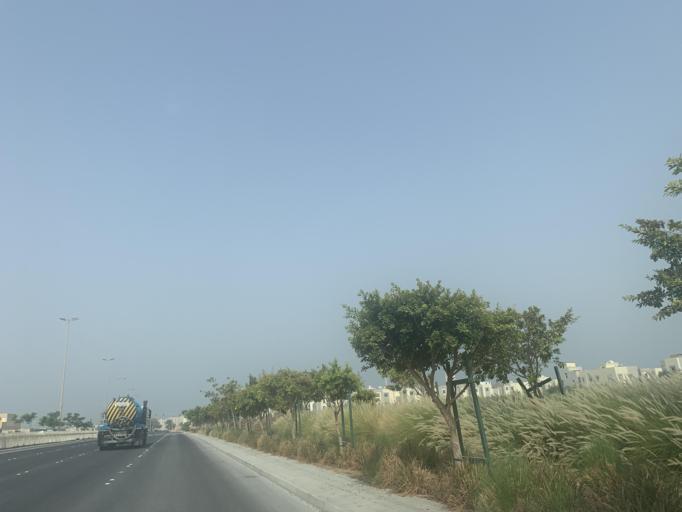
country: BH
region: Manama
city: Jidd Hafs
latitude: 26.2311
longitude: 50.4512
